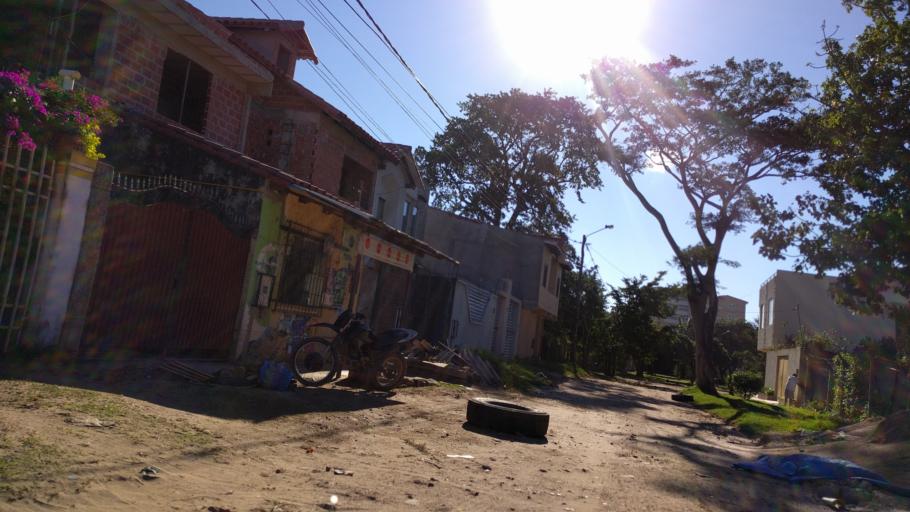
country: BO
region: Santa Cruz
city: Santa Cruz de la Sierra
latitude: -17.8045
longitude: -63.2240
